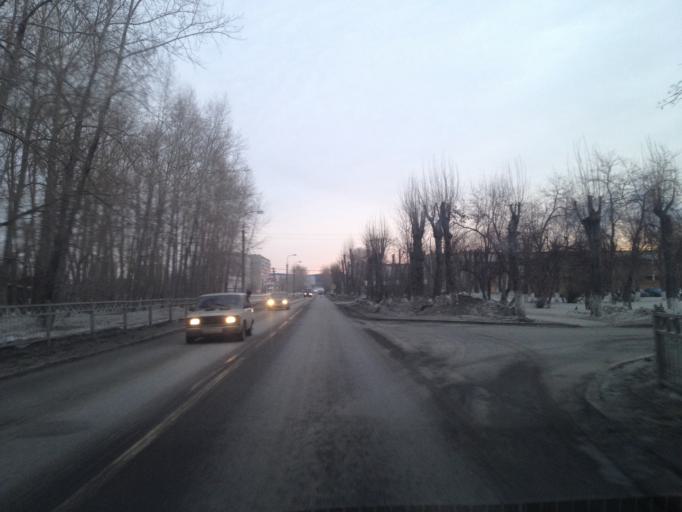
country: RU
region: Sverdlovsk
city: Sovkhoznyy
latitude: 56.7567
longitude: 60.5964
